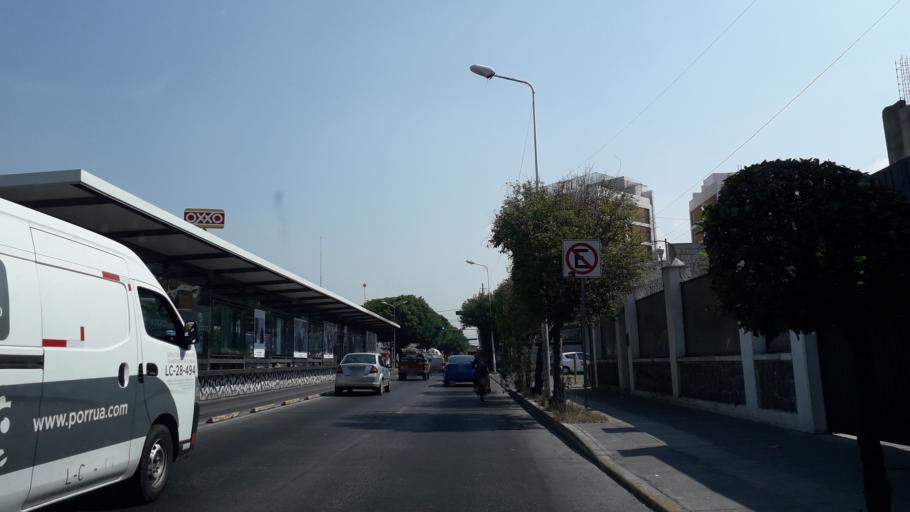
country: MX
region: Puebla
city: Puebla
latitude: 19.0408
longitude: -98.2105
